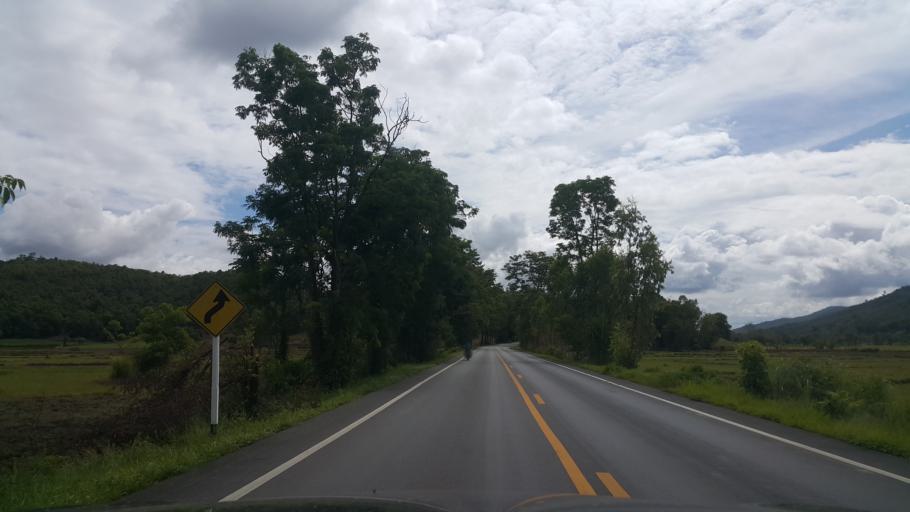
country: TH
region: Uttaradit
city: Thong Saen Khan
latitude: 17.3694
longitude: 100.2537
